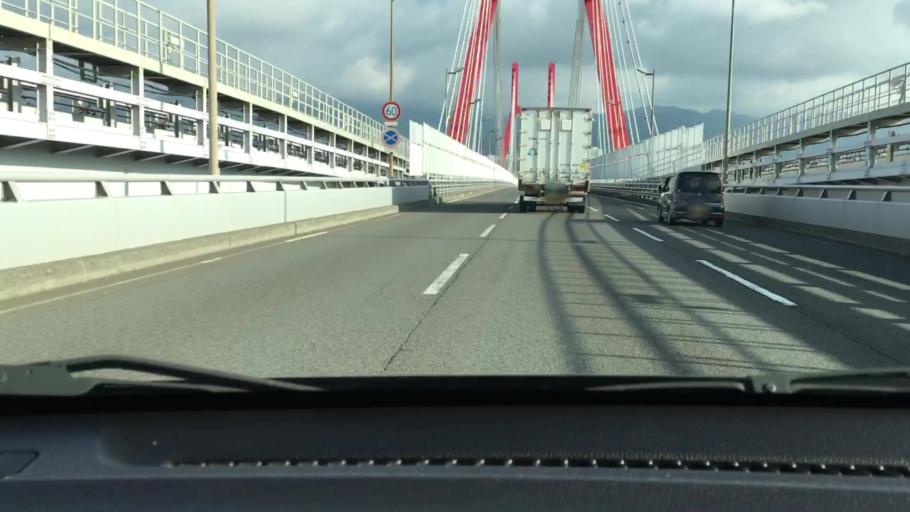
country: JP
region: Hyogo
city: Ashiya
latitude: 34.6976
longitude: 135.2680
